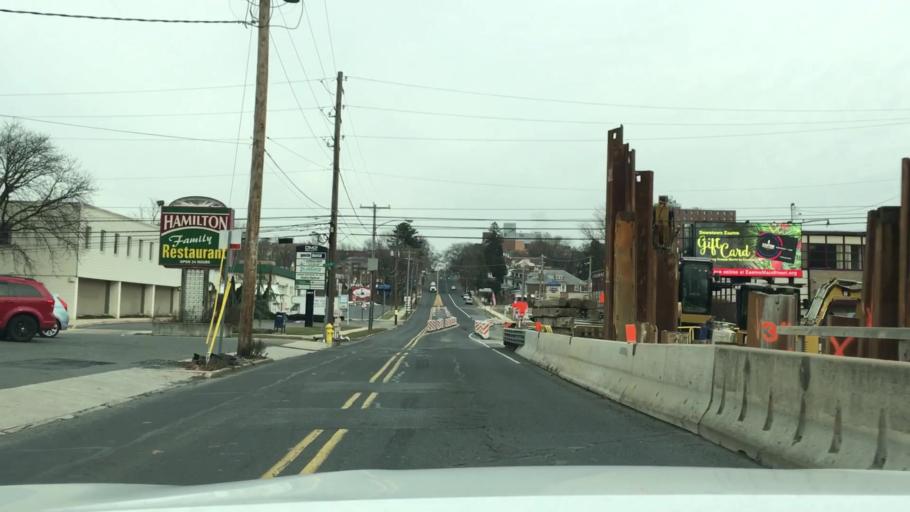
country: US
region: Pennsylvania
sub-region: Lehigh County
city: Allentown
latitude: 40.5945
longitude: -75.5000
